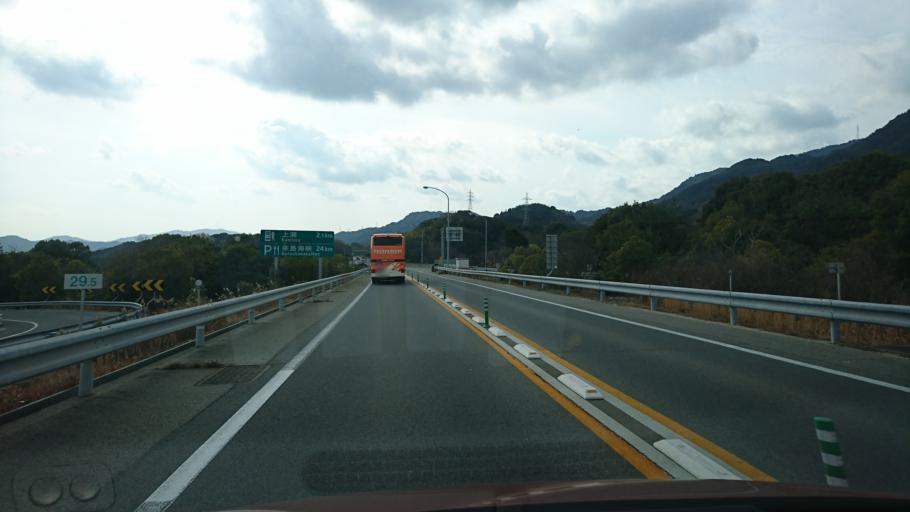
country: JP
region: Hiroshima
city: Innoshima
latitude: 34.2504
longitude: 133.0491
